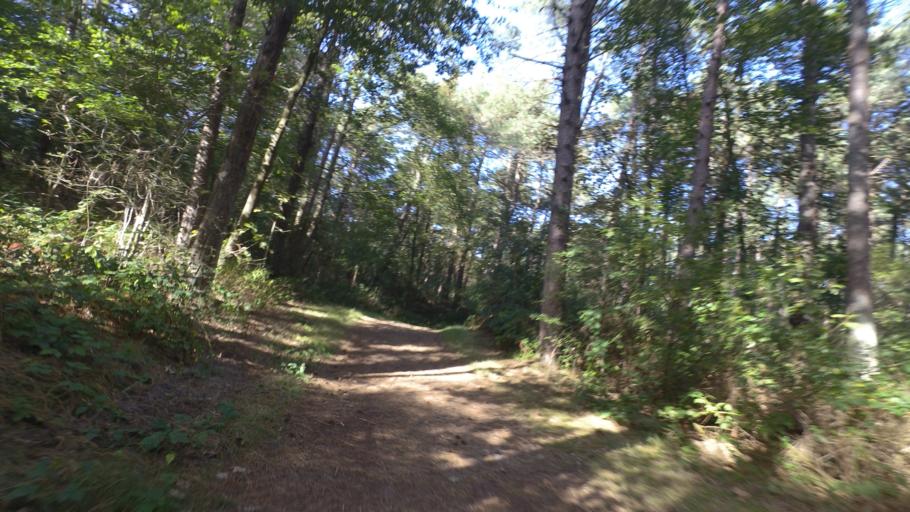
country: NL
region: Friesland
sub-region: Gemeente Ameland
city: Nes
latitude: 53.4528
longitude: 5.7633
